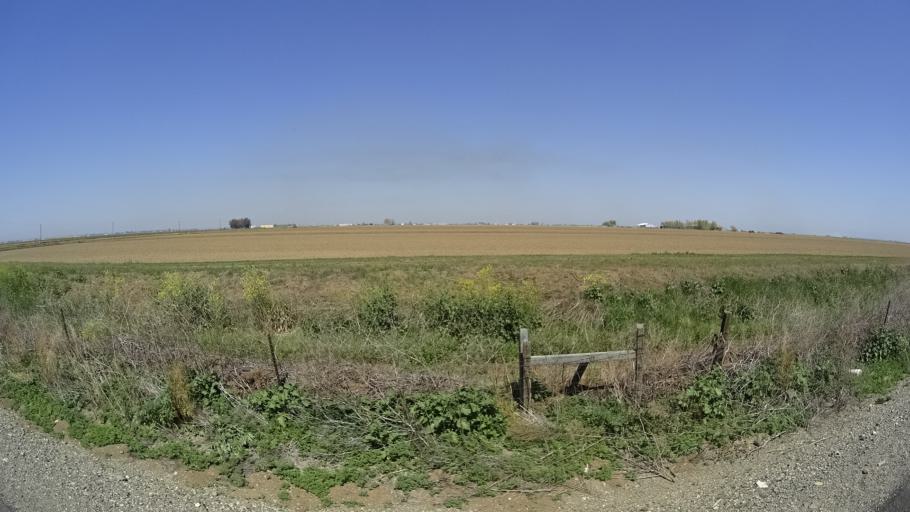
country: US
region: California
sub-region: Glenn County
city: Willows
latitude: 39.4647
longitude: -122.1344
